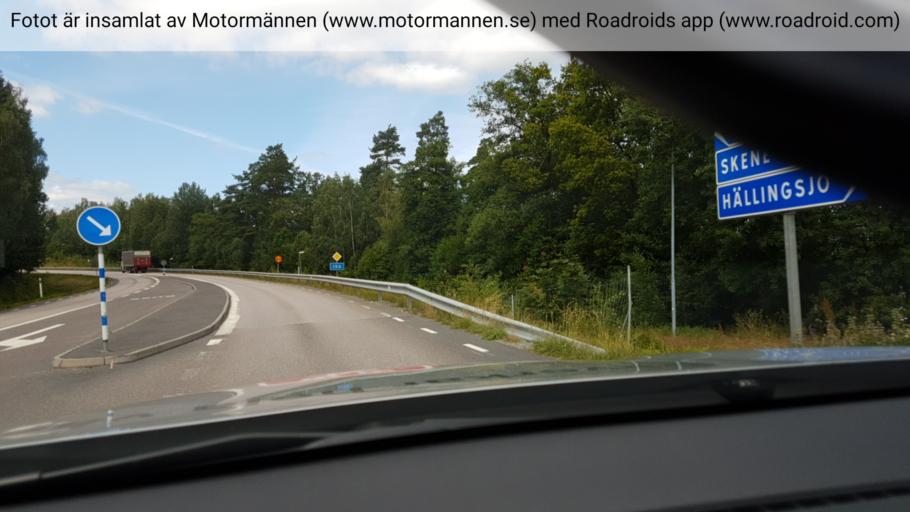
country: SE
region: Vaestra Goetaland
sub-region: Harryda Kommun
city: Ravlanda
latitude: 57.6198
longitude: 12.4338
